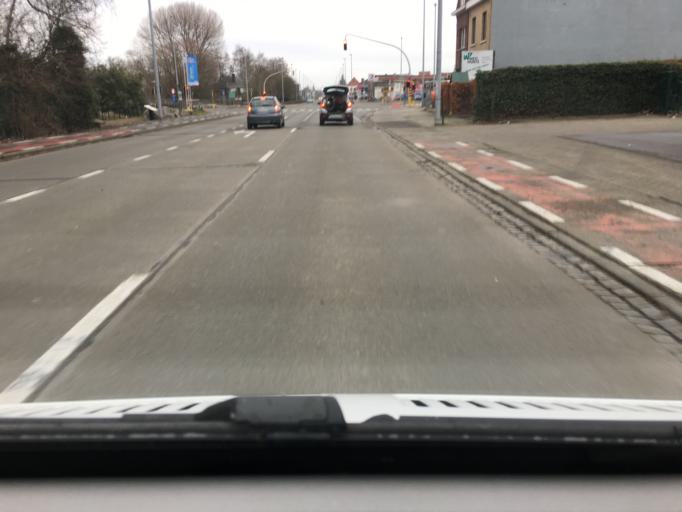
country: BE
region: Flanders
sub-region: Provincie West-Vlaanderen
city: Kuurne
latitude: 50.8382
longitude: 3.2849
